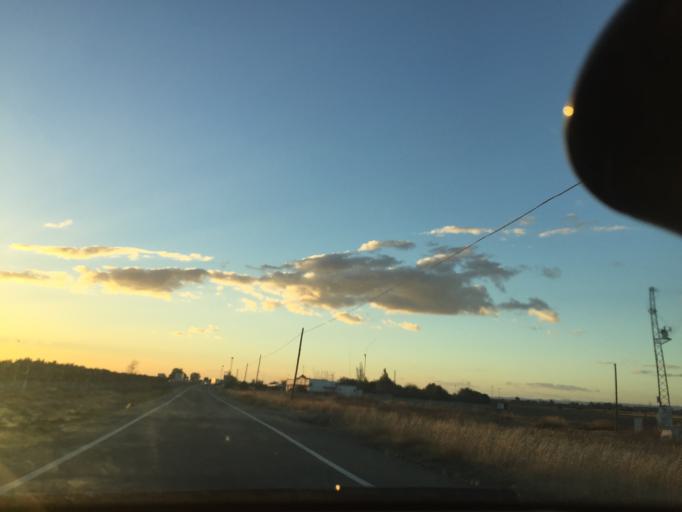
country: ES
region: Andalusia
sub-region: Provincia de Sevilla
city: Fuentes de Andalucia
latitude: 37.5068
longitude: -5.3853
